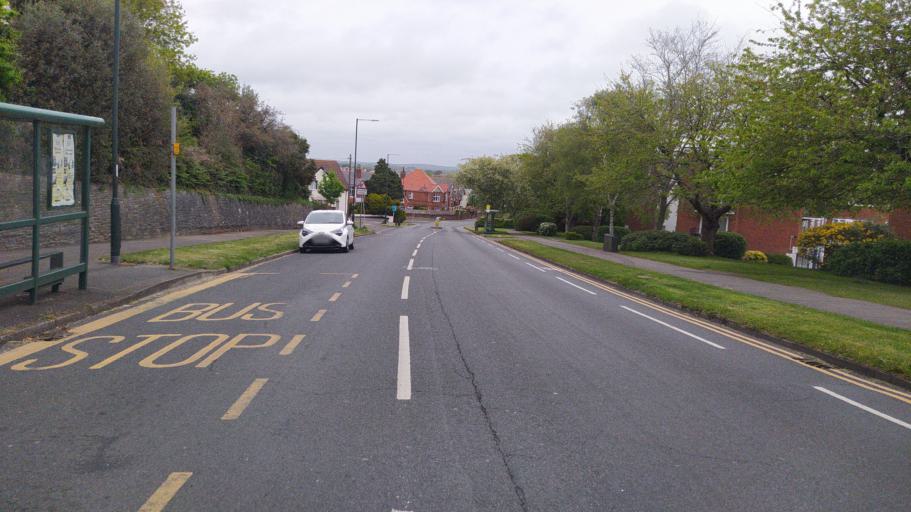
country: GB
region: England
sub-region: Dorset
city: Christchurch
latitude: 50.7249
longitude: -1.7941
